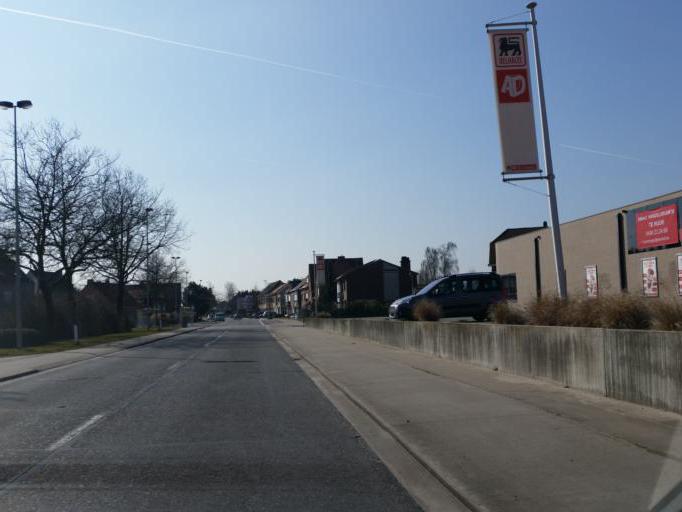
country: BE
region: Flanders
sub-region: Provincie Oost-Vlaanderen
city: Kruibeke
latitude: 51.1630
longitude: 4.3068
